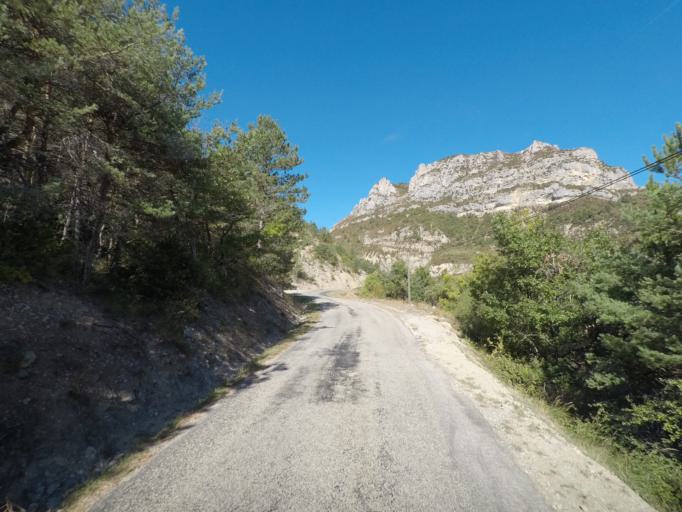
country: FR
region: Rhone-Alpes
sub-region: Departement de la Drome
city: Buis-les-Baronnies
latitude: 44.5046
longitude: 5.3475
